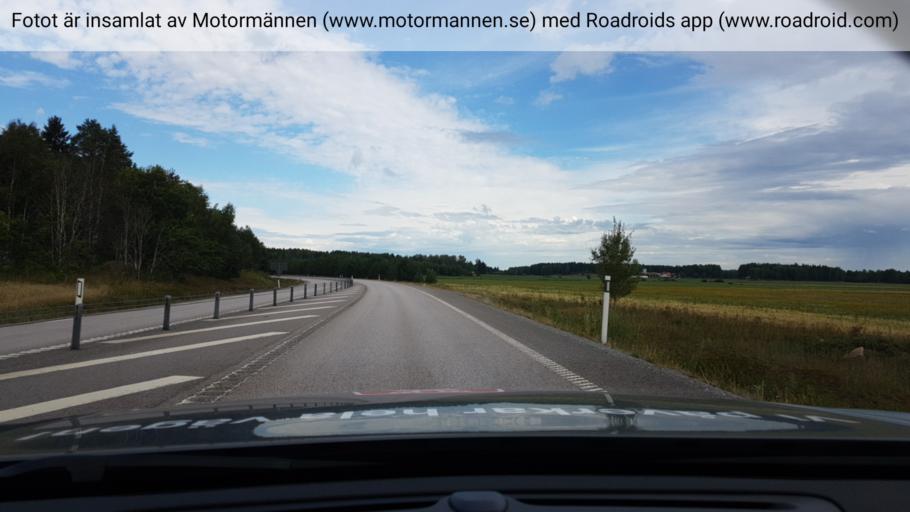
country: SE
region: Uppsala
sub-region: Heby Kommun
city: Tarnsjo
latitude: 60.2518
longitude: 16.9599
